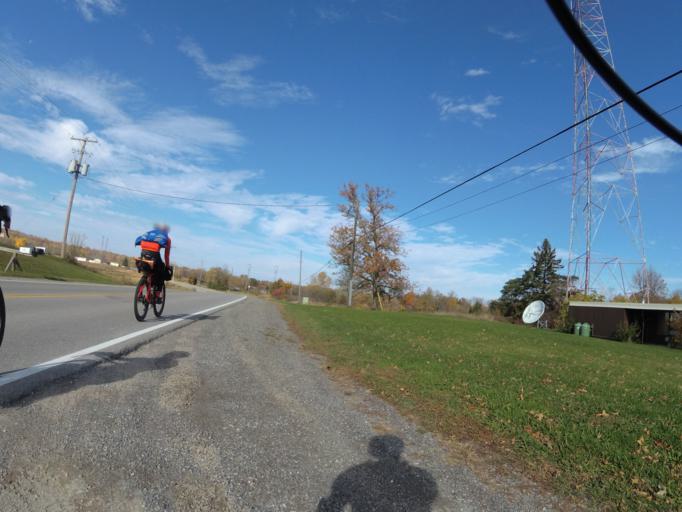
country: CA
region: Ontario
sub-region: Lanark County
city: Smiths Falls
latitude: 44.8910
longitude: -76.0116
